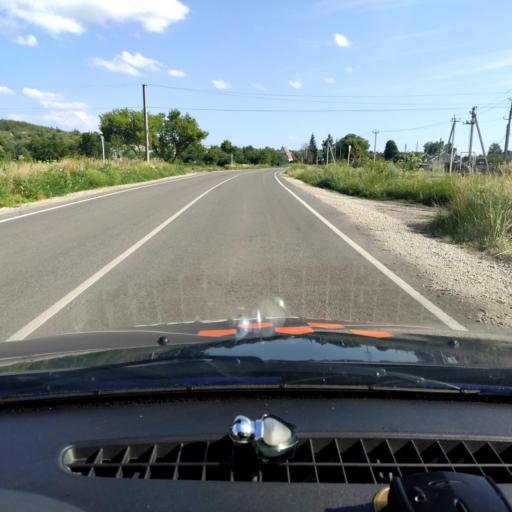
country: RU
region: Voronezj
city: Devitsa
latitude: 51.6524
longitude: 38.9724
